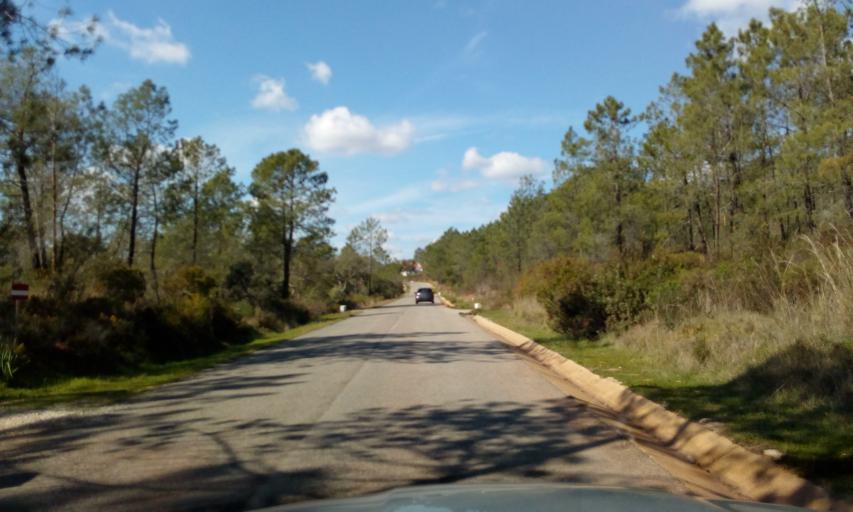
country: PT
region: Faro
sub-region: Loule
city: Loule
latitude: 37.2459
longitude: -8.0743
